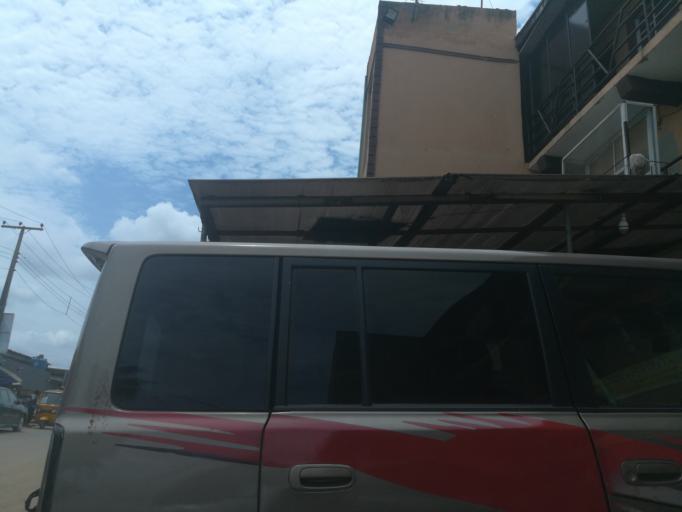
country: NG
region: Lagos
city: Somolu
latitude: 6.5240
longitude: 3.3853
